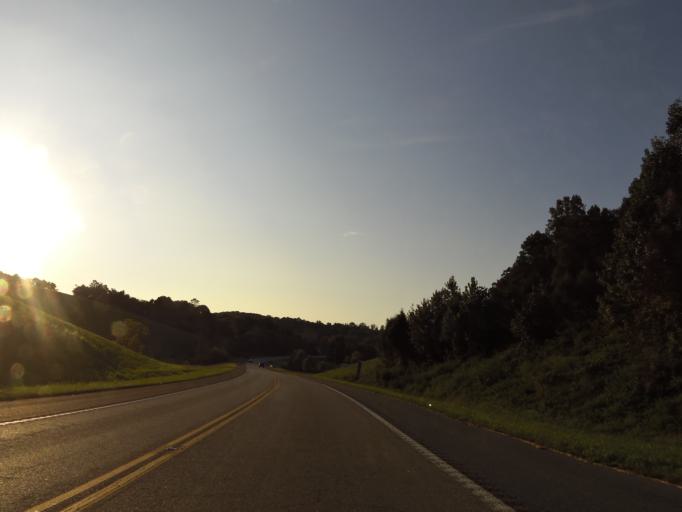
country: US
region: Tennessee
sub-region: Meigs County
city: Decatur
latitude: 35.5724
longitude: -84.6720
